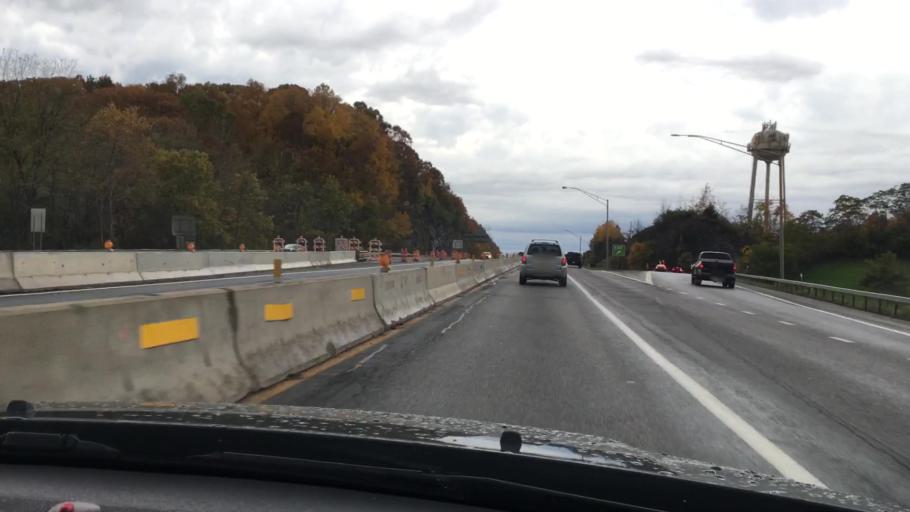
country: US
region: New York
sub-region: Orange County
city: Balmville
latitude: 41.5196
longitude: -74.0220
